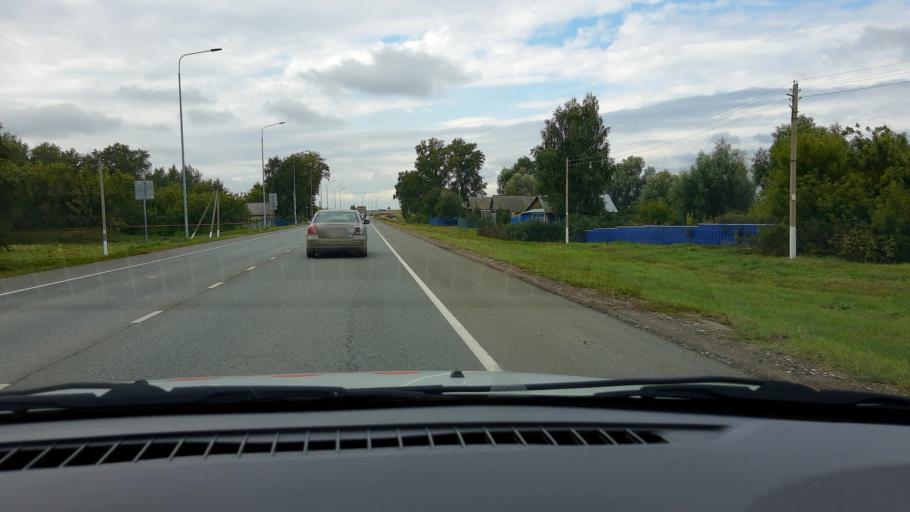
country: RU
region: Tatarstan
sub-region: Alekseyevskiy Rayon
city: Alekseyevskoye
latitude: 55.3105
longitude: 50.3003
